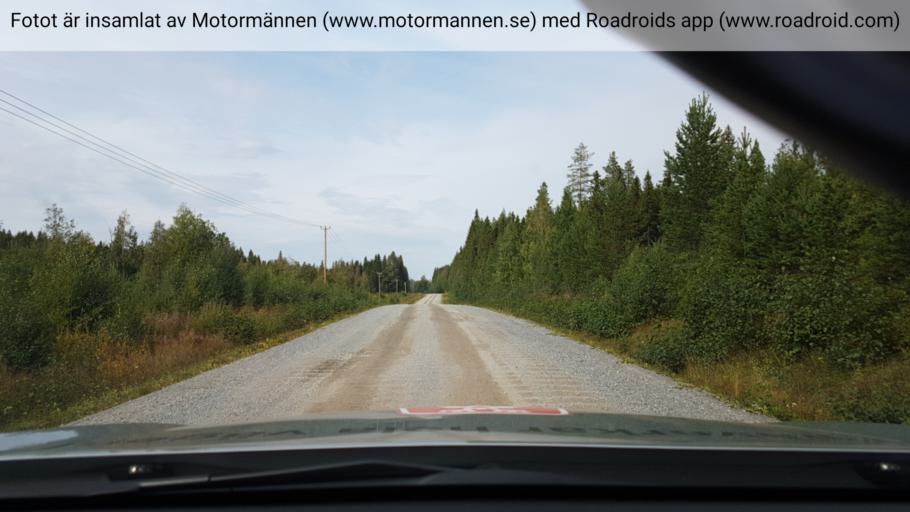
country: SE
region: Vaesterbotten
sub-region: Bjurholms Kommun
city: Bjurholm
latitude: 63.9278
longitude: 19.3634
